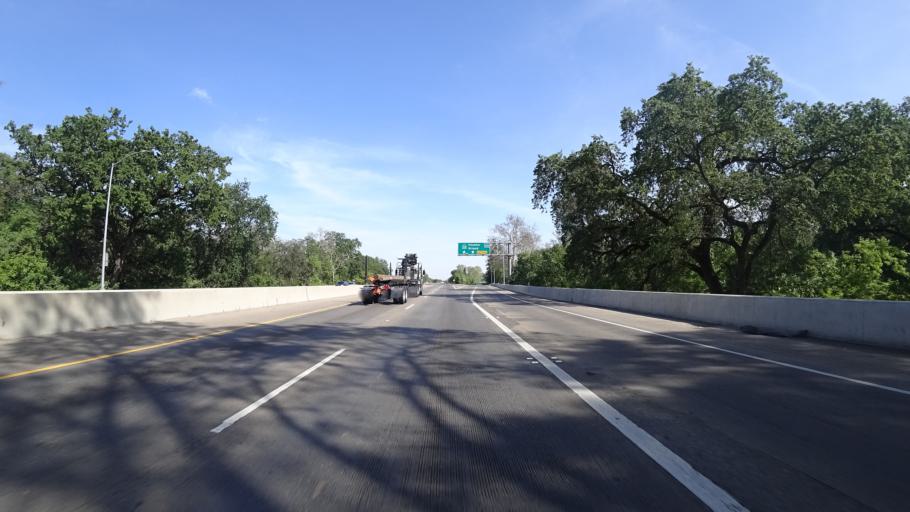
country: US
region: California
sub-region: Butte County
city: Chico
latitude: 39.7394
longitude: -121.8237
